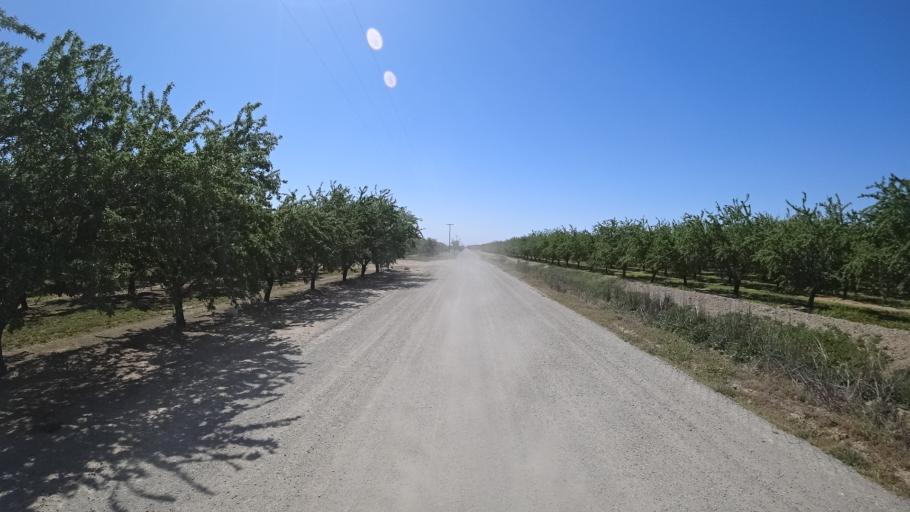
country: US
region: California
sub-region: Glenn County
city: Orland
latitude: 39.6923
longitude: -122.1591
